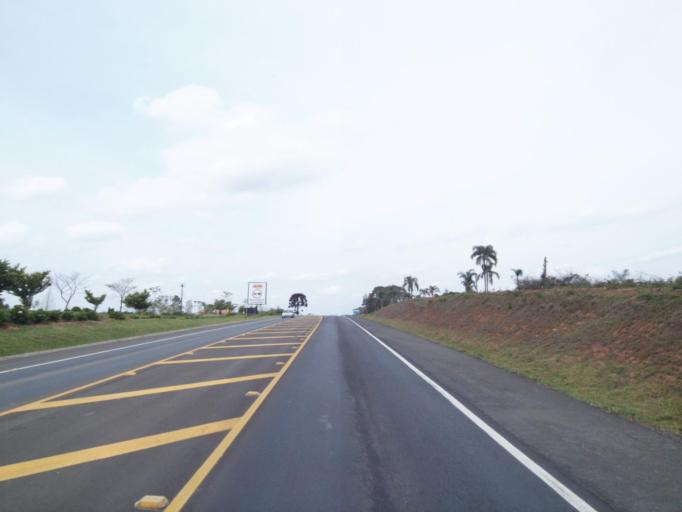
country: BR
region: Parana
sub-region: Irati
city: Irati
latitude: -25.4646
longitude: -50.5718
